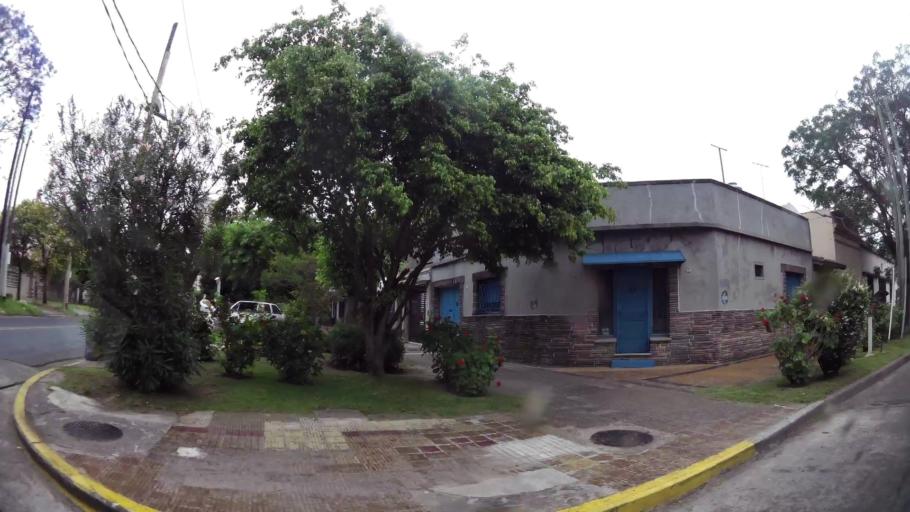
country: AR
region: Buenos Aires
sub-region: Partido de Lanus
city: Lanus
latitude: -34.6967
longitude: -58.3959
